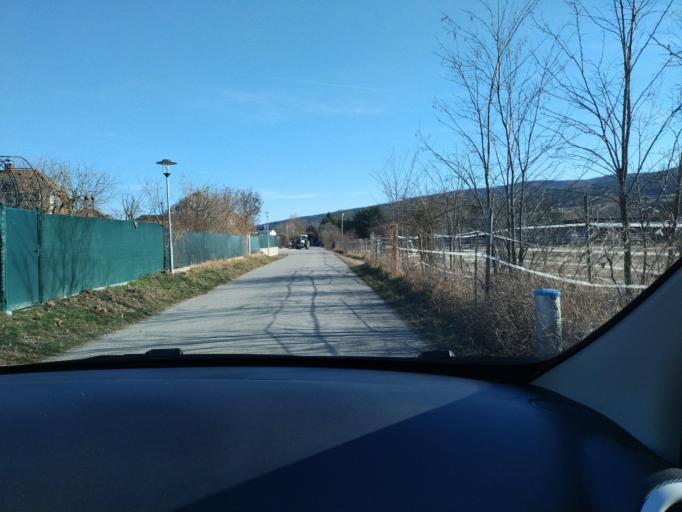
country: AT
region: Lower Austria
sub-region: Politischer Bezirk Wiener Neustadt
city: Lanzenkirchen
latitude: 47.7498
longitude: 16.2550
